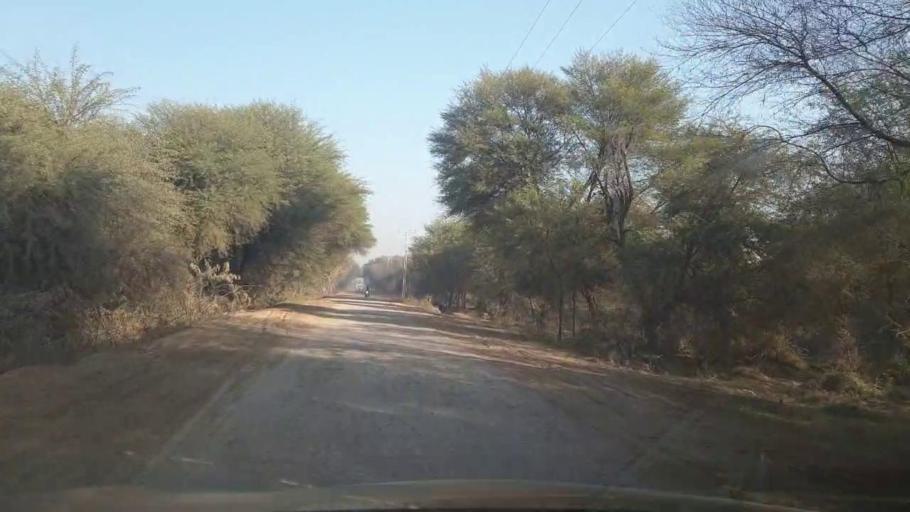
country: PK
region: Sindh
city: Mirpur Mathelo
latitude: 28.0612
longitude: 69.4640
